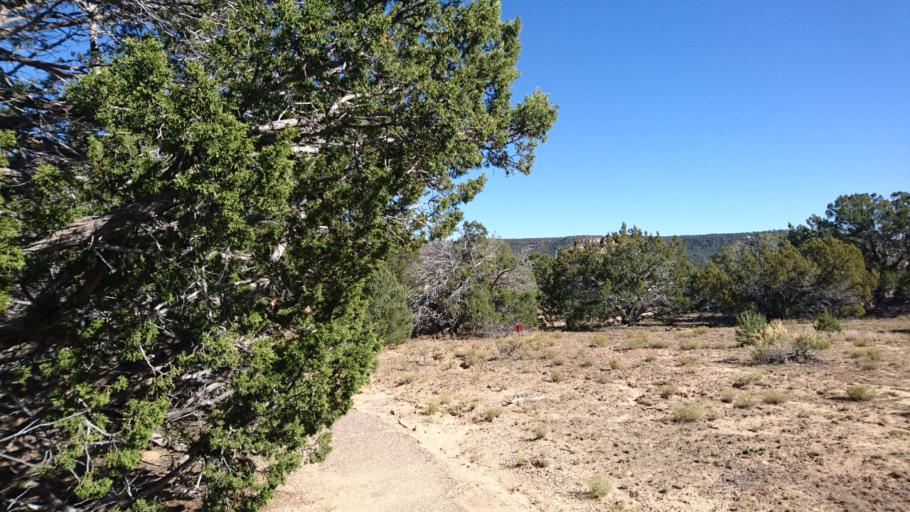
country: US
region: New Mexico
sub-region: McKinley County
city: Thoreau
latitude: 35.0385
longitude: -108.3497
